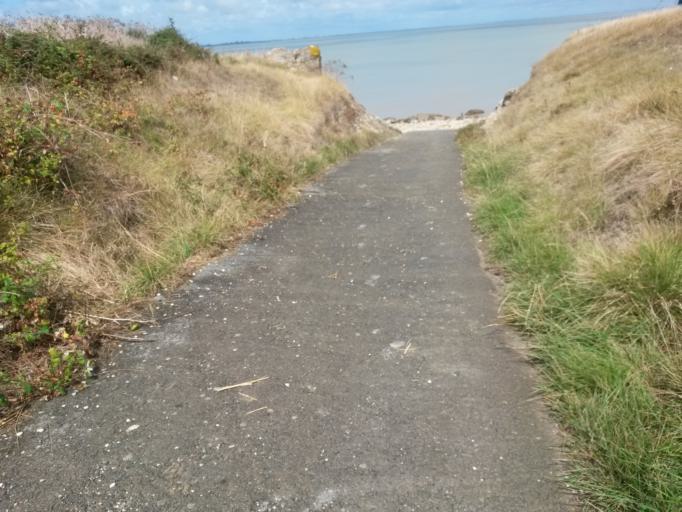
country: FR
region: Poitou-Charentes
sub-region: Departement de la Charente-Maritime
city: Nieul-sur-Mer
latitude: 46.2220
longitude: -1.1739
